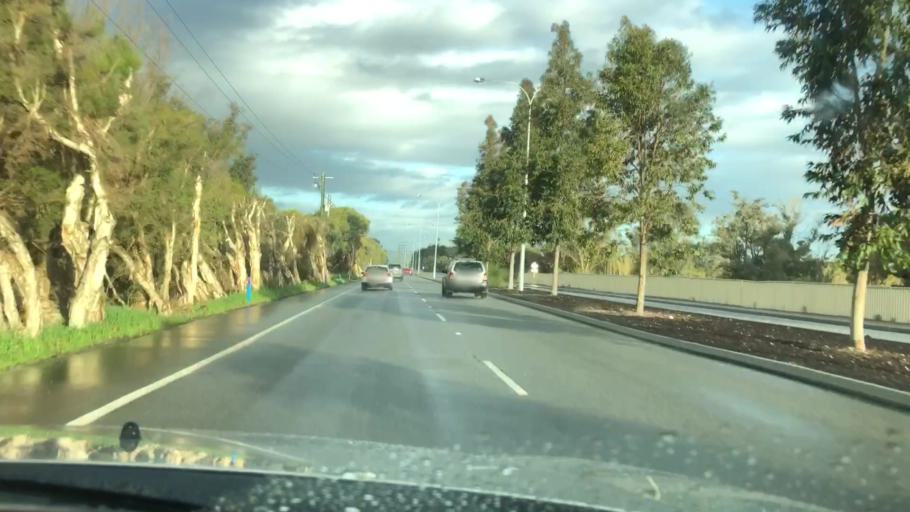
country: AU
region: Western Australia
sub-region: Armadale
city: Harrisdale
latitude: -32.1109
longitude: 115.9428
